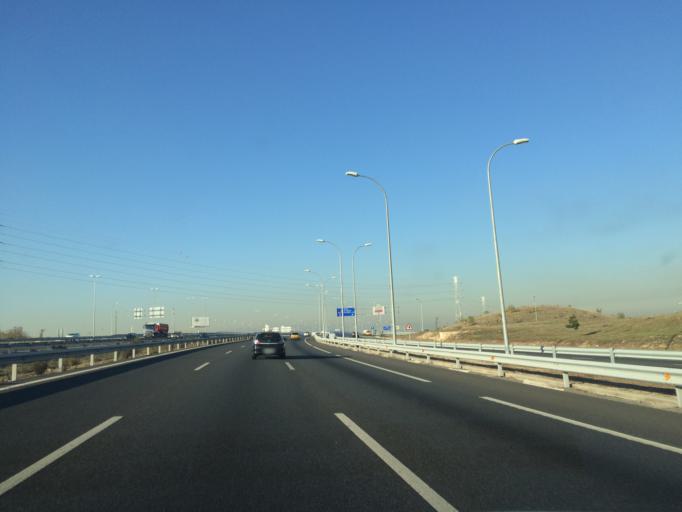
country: ES
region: Madrid
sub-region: Provincia de Madrid
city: Pozuelo de Alarcon
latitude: 40.3943
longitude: -3.8325
